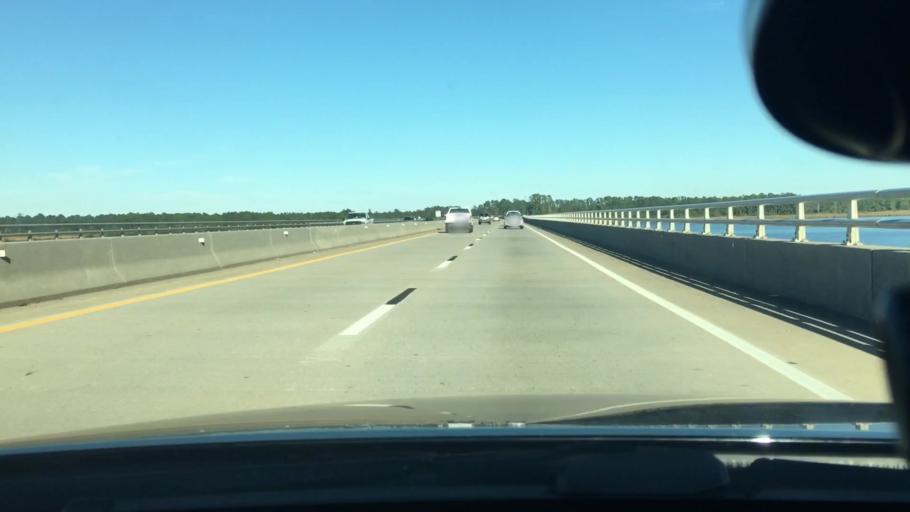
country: US
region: North Carolina
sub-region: Craven County
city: James City
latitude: 35.0990
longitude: -77.0184
